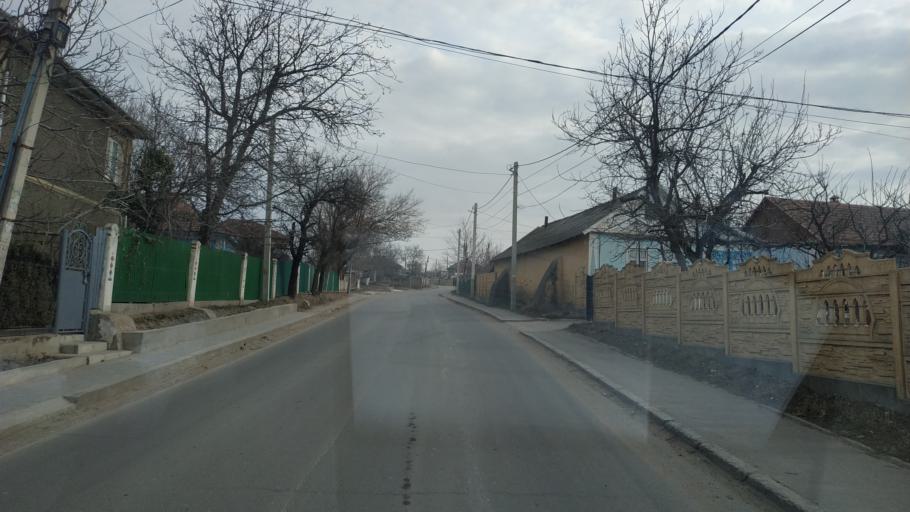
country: MD
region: Chisinau
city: Singera
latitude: 46.9641
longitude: 29.0572
